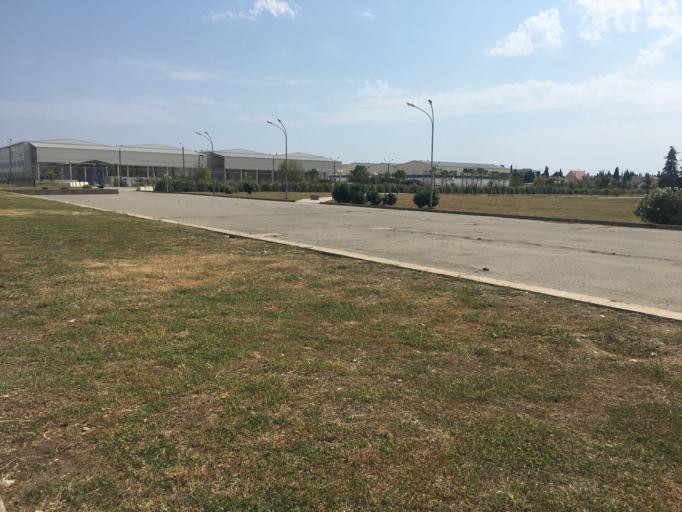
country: RU
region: Krasnodarskiy
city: Adler
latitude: 43.3987
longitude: 39.9822
